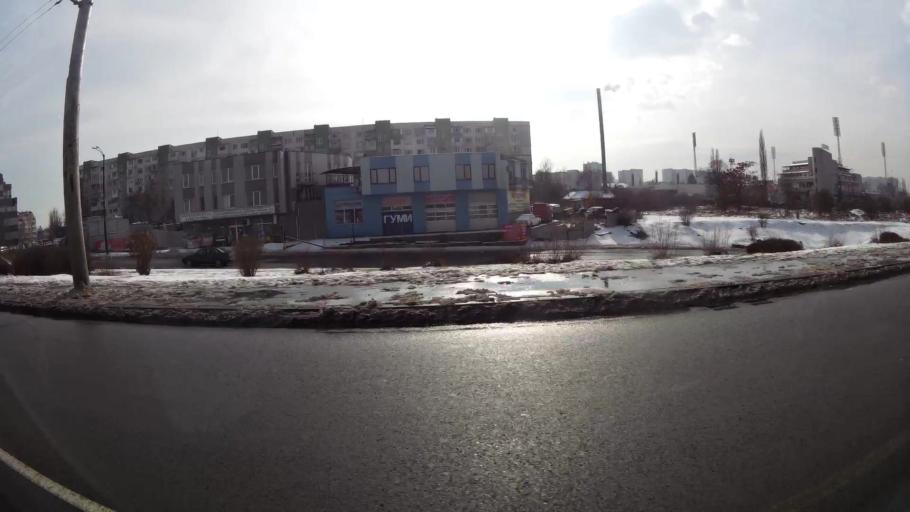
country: BG
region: Sofia-Capital
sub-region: Stolichna Obshtina
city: Sofia
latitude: 42.7088
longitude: 23.3672
